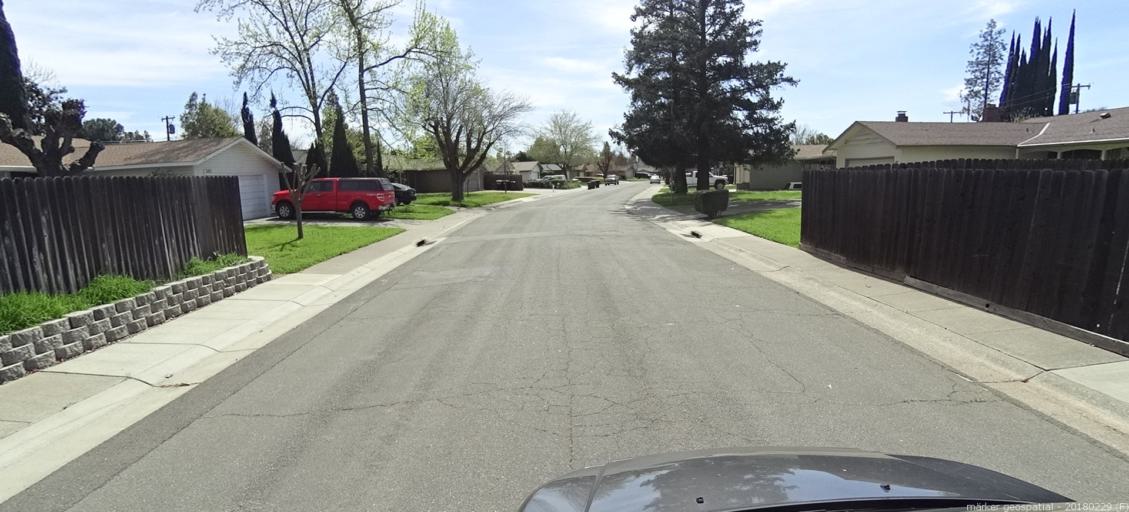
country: US
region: California
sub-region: Sacramento County
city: Rosemont
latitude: 38.5517
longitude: -121.3588
